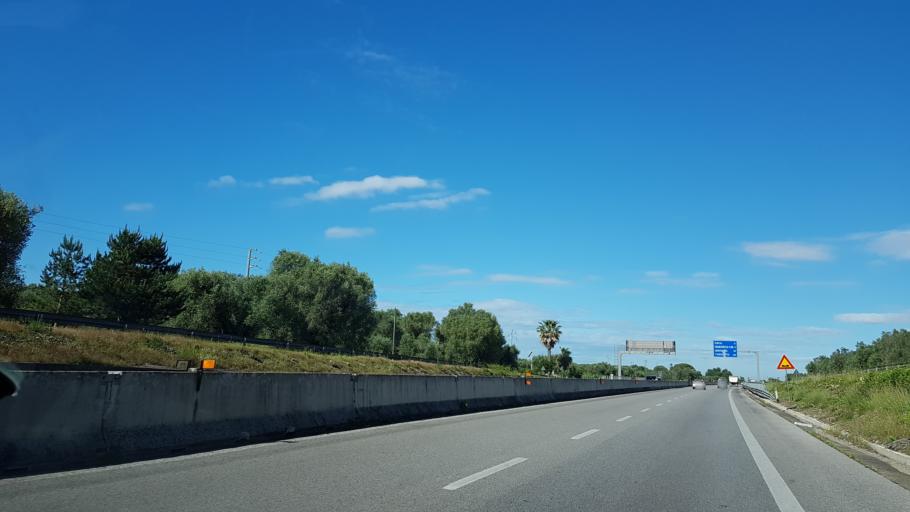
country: IT
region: Apulia
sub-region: Provincia di Brindisi
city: Latiano
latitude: 40.5432
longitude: 17.6784
